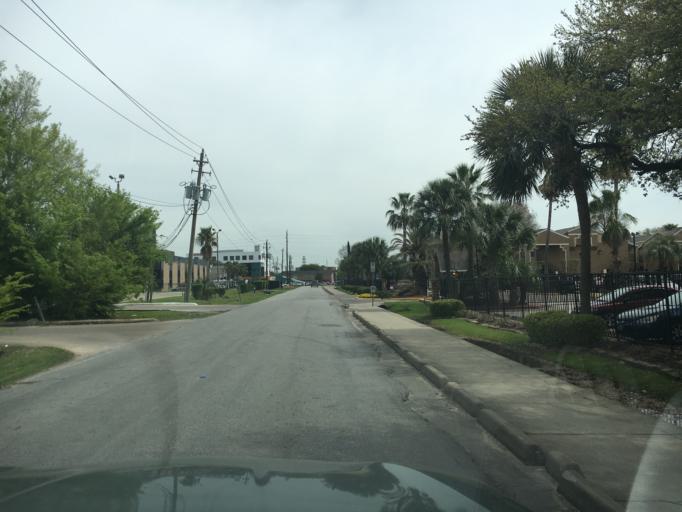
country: US
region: Texas
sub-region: Harris County
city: Bellaire
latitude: 29.7307
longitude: -95.4869
